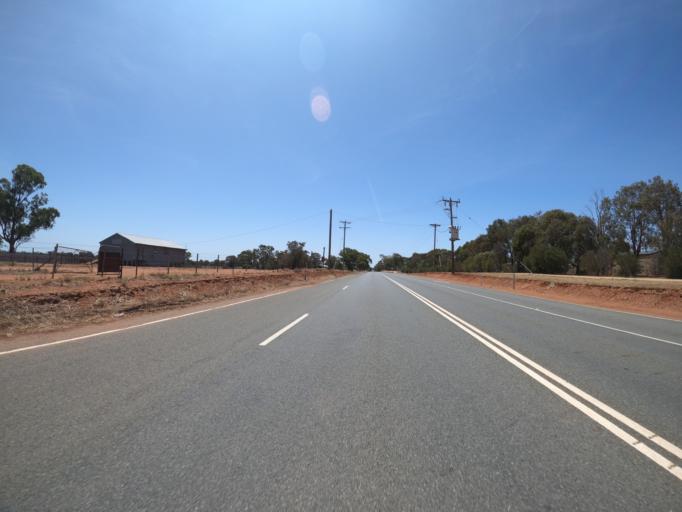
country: AU
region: Victoria
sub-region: Moira
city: Yarrawonga
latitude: -36.0479
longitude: 145.9955
